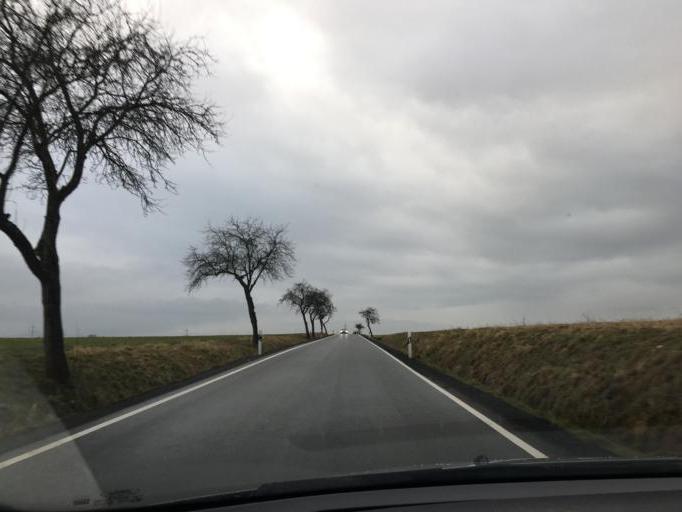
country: DE
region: Saxony
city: Pfaffroda
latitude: 50.8899
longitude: 12.5382
